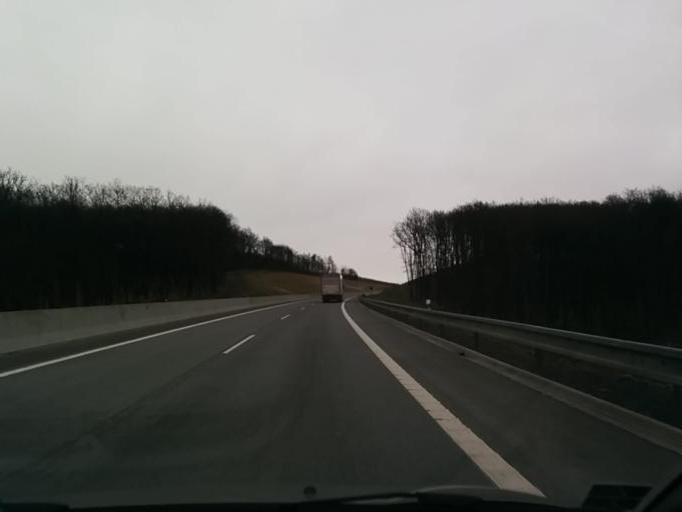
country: SK
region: Nitriansky
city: Tlmace
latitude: 48.3723
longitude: 18.5127
